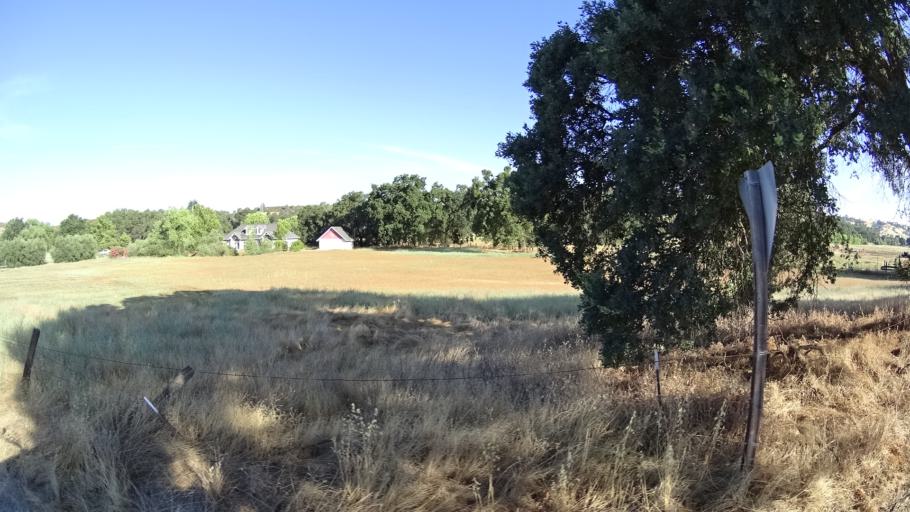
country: US
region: California
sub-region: Calaveras County
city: Valley Springs
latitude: 38.2065
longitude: -120.7895
